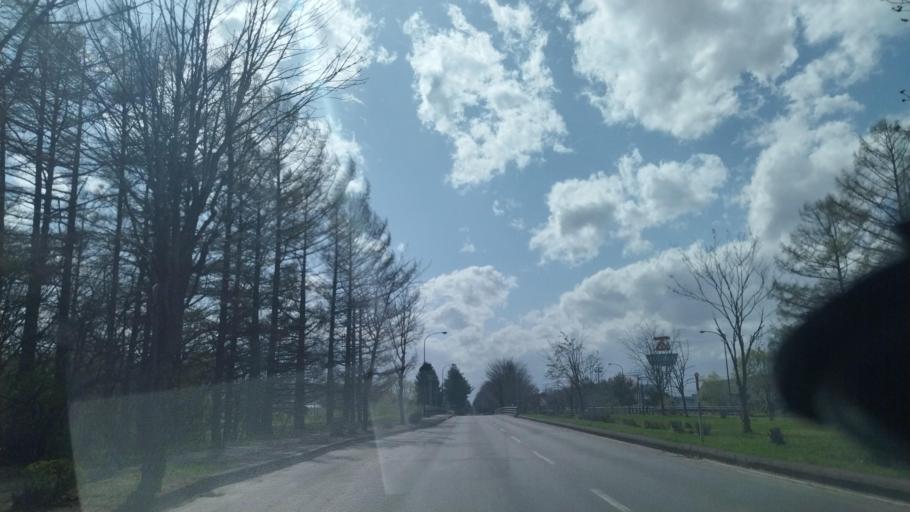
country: JP
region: Hokkaido
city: Obihiro
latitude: 42.9301
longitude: 143.1425
